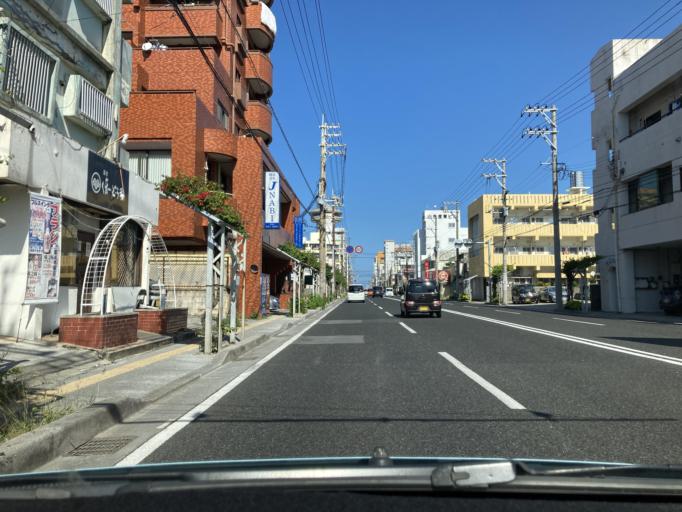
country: JP
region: Okinawa
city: Naha-shi
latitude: 26.2373
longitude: 127.6816
